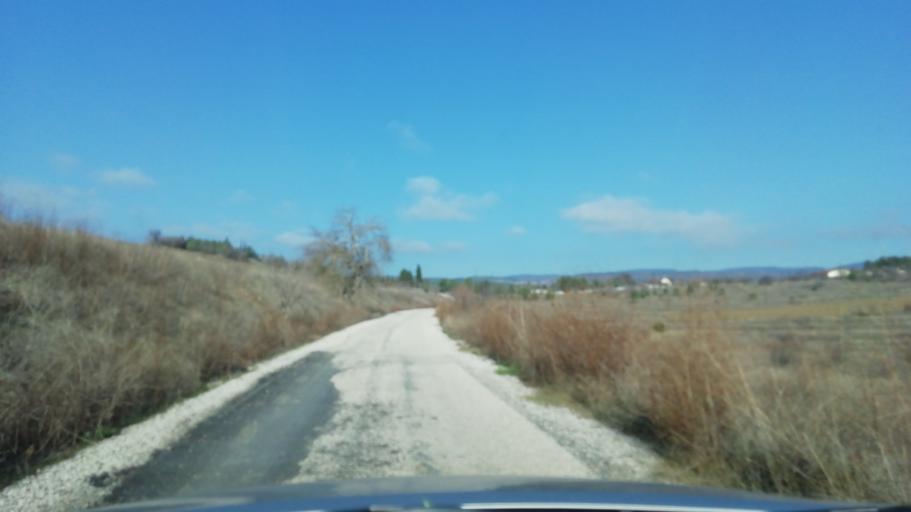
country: TR
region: Karabuk
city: Safranbolu
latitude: 41.2266
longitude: 32.7761
